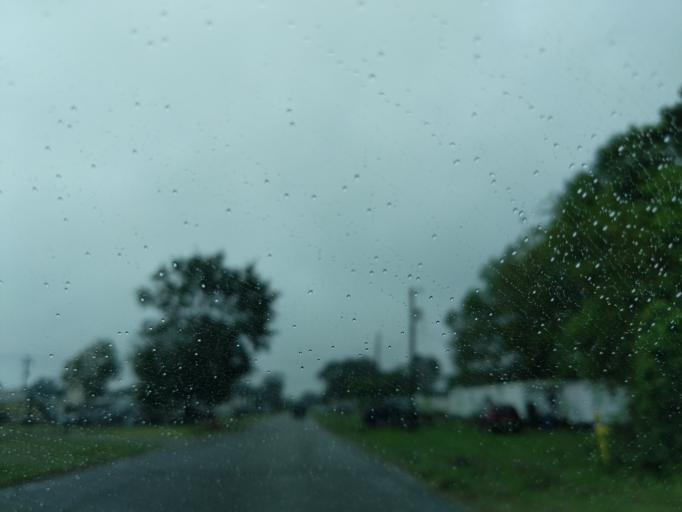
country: US
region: Louisiana
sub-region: Vermilion Parish
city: Kaplan
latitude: 29.9961
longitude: -92.2815
